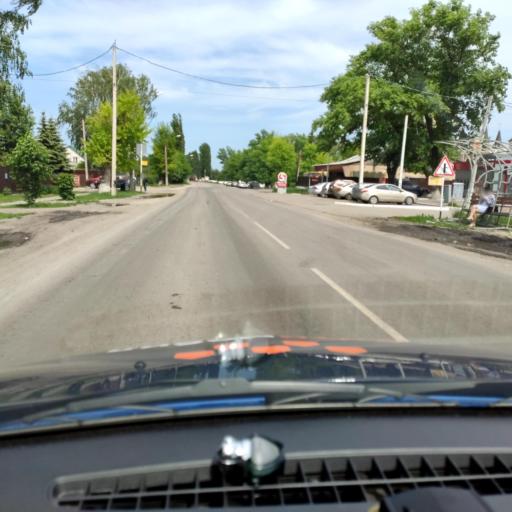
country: RU
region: Voronezj
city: Maslovka
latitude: 51.5393
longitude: 39.3400
